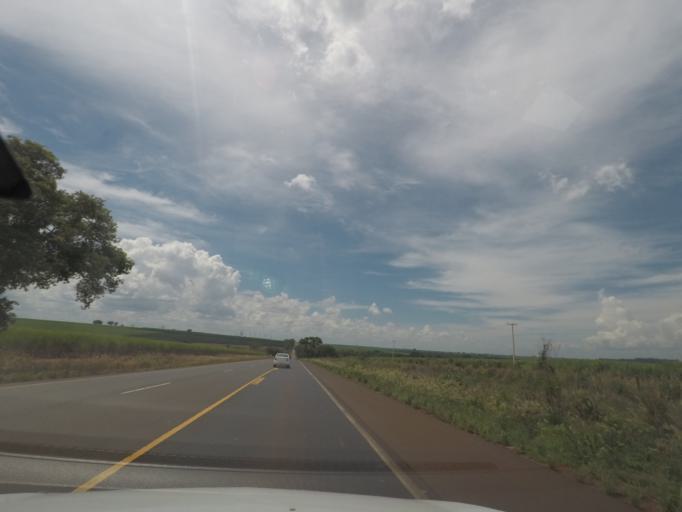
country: BR
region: Sao Paulo
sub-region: Barretos
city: Barretos
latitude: -20.2666
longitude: -48.6739
